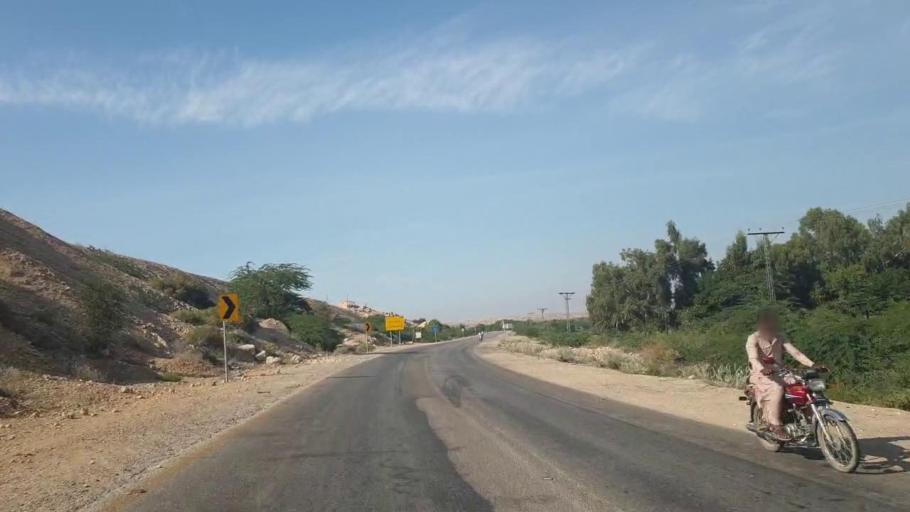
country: PK
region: Sindh
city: Sehwan
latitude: 26.3237
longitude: 67.8841
